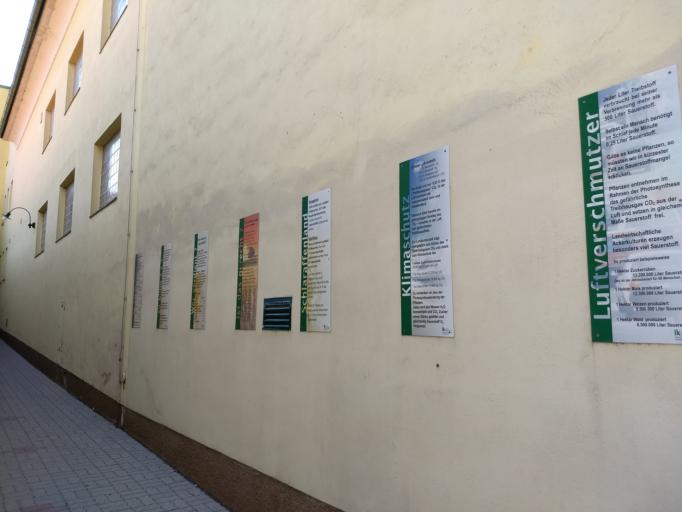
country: AT
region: Lower Austria
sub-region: Politischer Bezirk Mistelbach
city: Poysdorf
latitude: 48.6684
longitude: 16.6282
